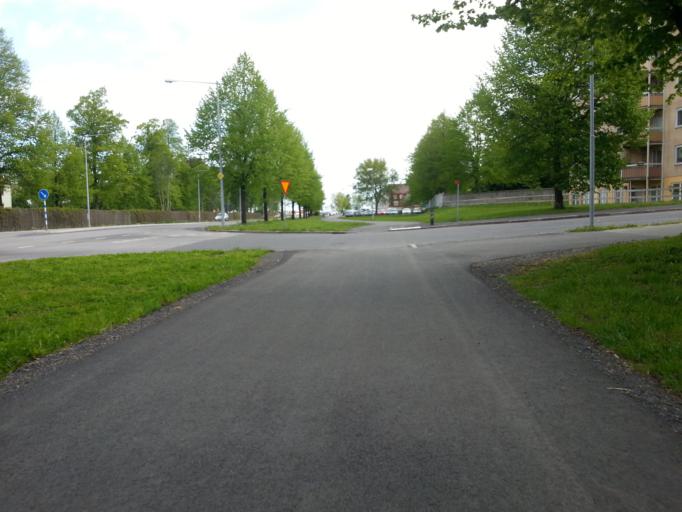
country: SE
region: Joenkoeping
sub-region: Jonkopings Kommun
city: Jonkoping
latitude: 57.7827
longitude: 14.1529
